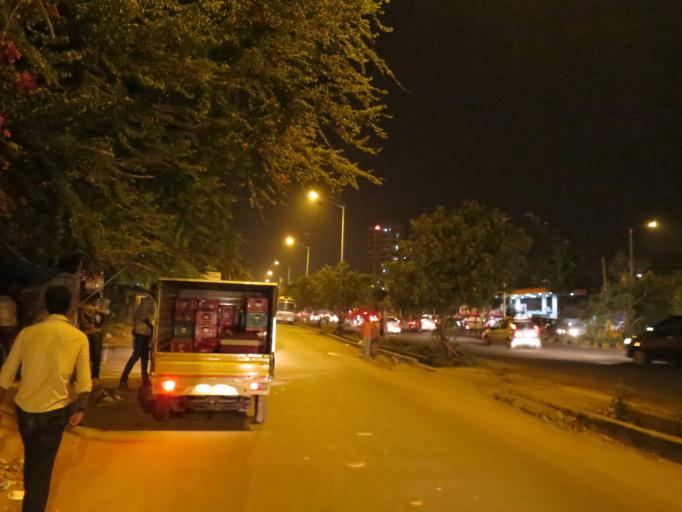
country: IN
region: Karnataka
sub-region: Bangalore Urban
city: Bangalore
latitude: 12.9862
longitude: 77.6903
